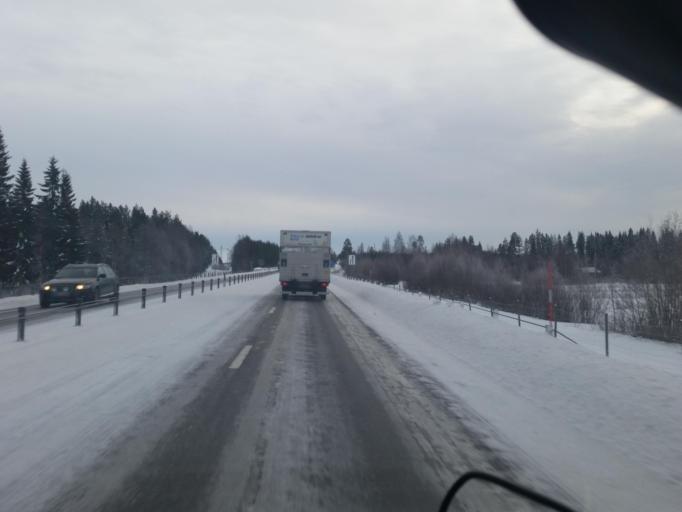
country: SE
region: Norrbotten
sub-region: Pitea Kommun
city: Pitea
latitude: 65.2465
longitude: 21.4853
